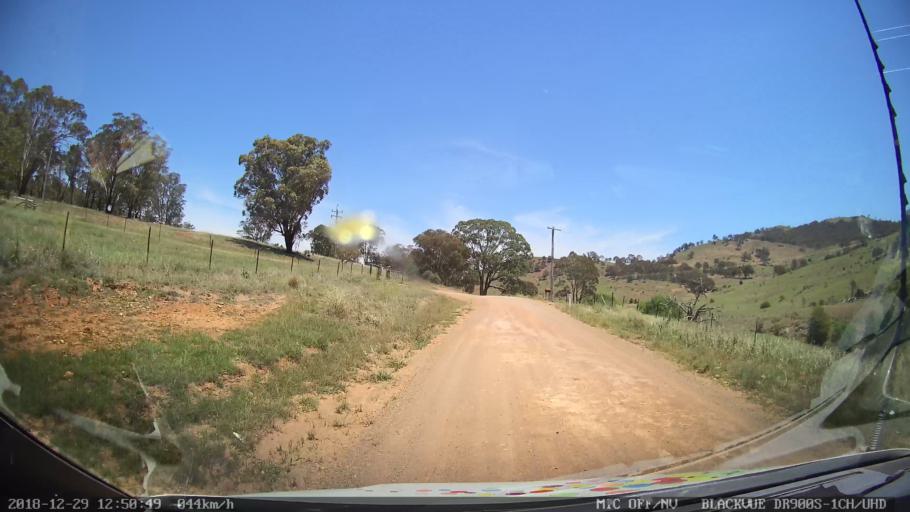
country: AU
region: Australian Capital Territory
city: Macarthur
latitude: -35.6721
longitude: 149.2015
